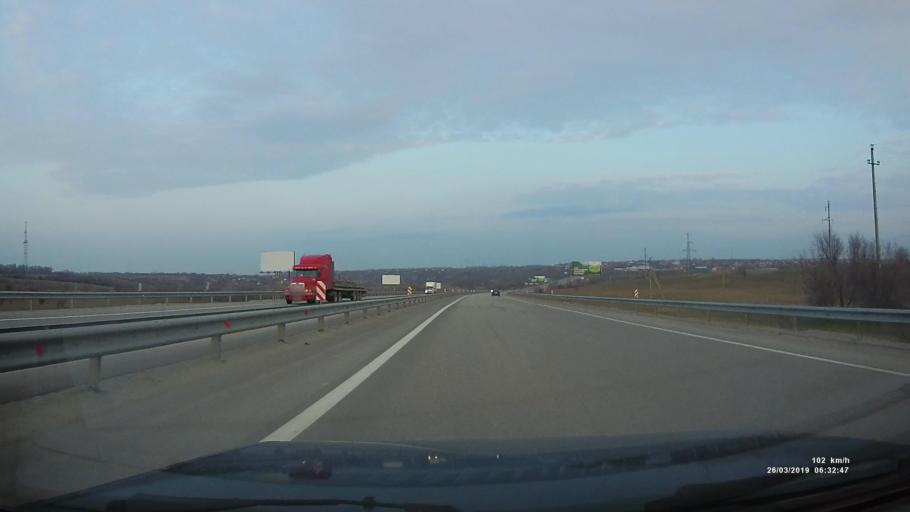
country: RU
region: Rostov
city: Chaltyr
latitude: 47.2702
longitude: 39.5024
